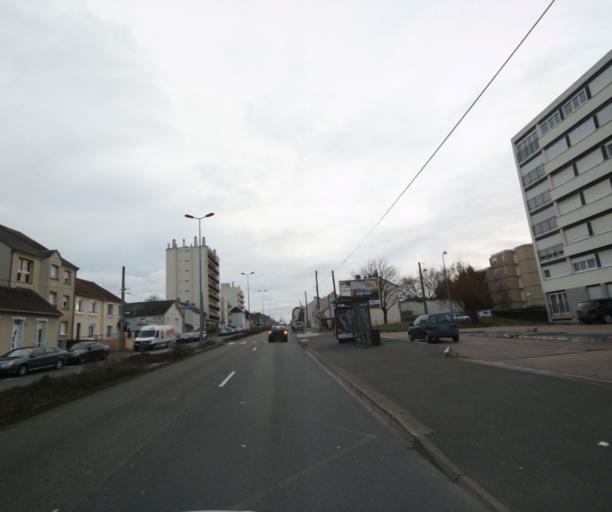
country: FR
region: Pays de la Loire
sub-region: Departement de la Sarthe
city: Le Mans
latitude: 47.9739
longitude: 0.2061
